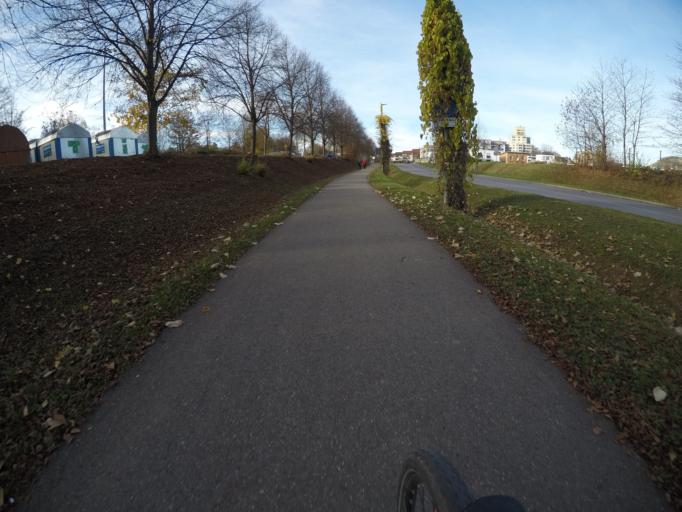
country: DE
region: Baden-Wuerttemberg
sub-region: Regierungsbezirk Stuttgart
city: Weinstadt-Endersbach
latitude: 48.8080
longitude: 9.3775
